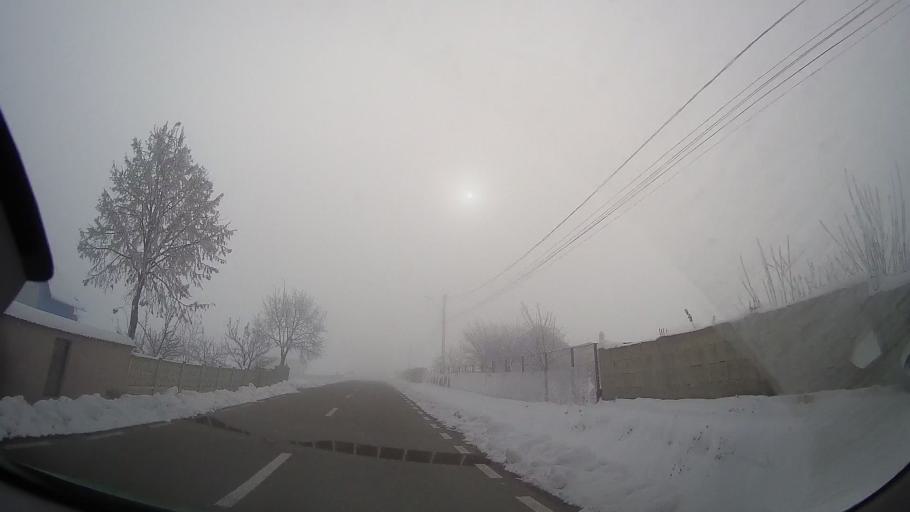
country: RO
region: Iasi
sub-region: Comuna Valea Seaca
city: Valea Seaca
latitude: 47.2816
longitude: 26.6700
